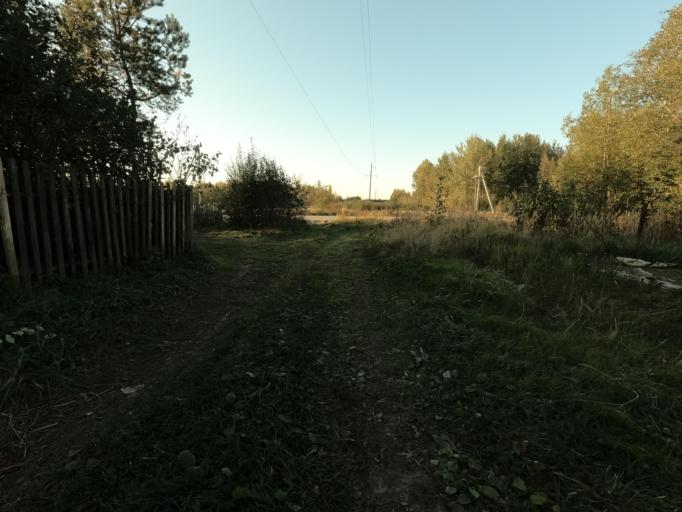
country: RU
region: Leningrad
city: Nikol'skoye
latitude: 59.7159
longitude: 30.7965
